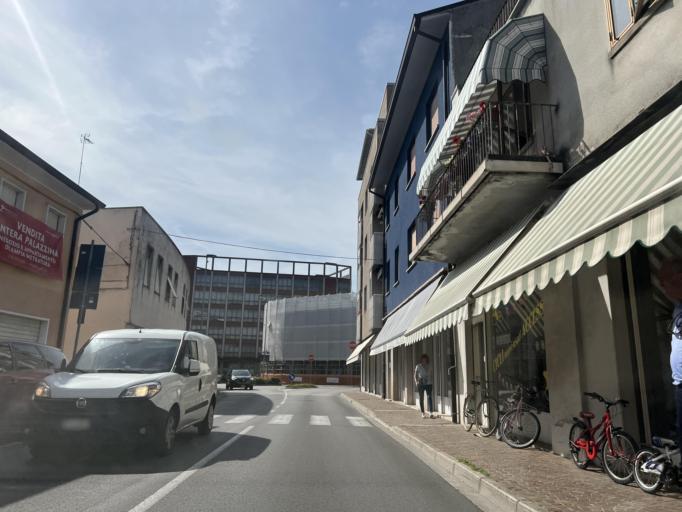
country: IT
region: Friuli Venezia Giulia
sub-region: Provincia di Udine
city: Cervignano del Friuli
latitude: 45.8227
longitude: 13.3391
